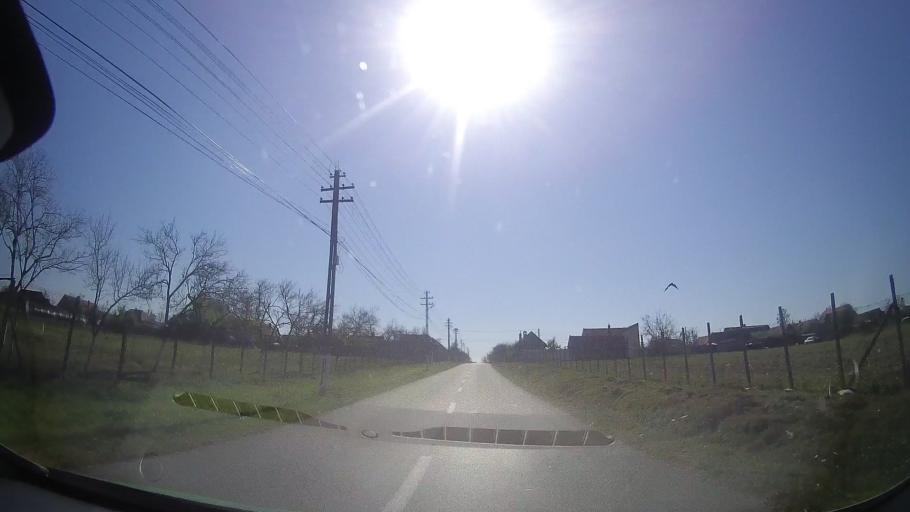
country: RO
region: Timis
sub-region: Comuna Bethausen
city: Bethausen
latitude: 45.7967
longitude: 21.9645
